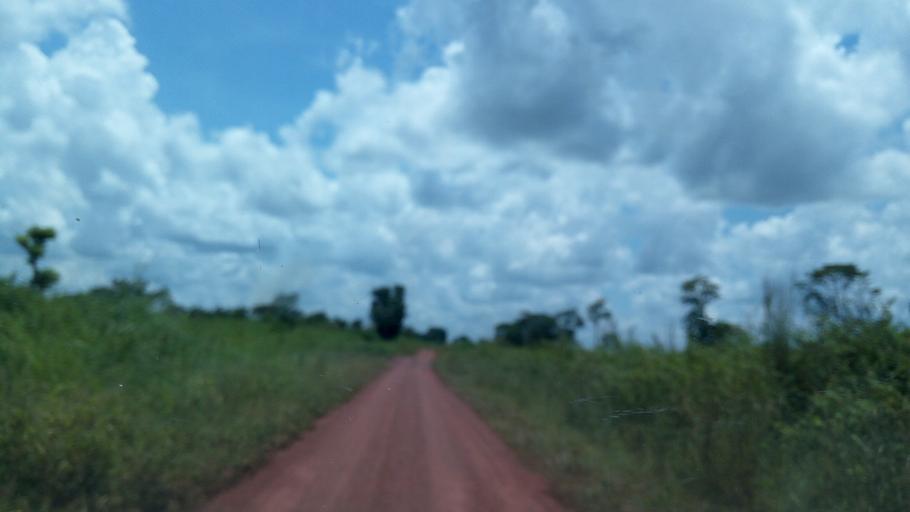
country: CD
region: Equateur
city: Libenge
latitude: 3.7729
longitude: 18.9422
